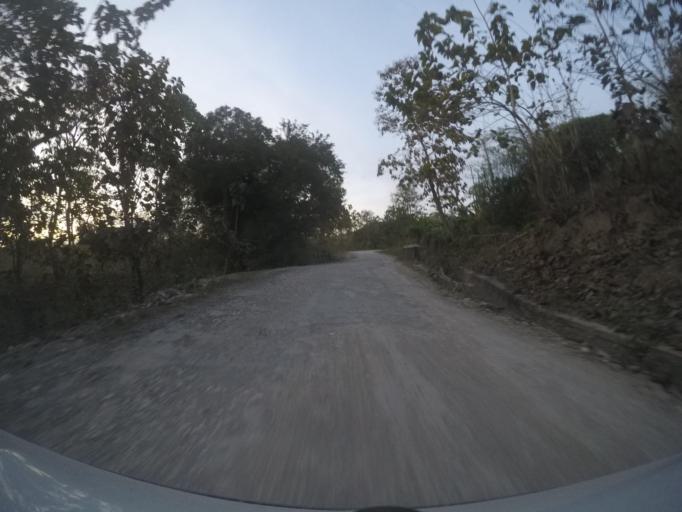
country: TL
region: Viqueque
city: Viqueque
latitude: -8.8876
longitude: 126.3861
